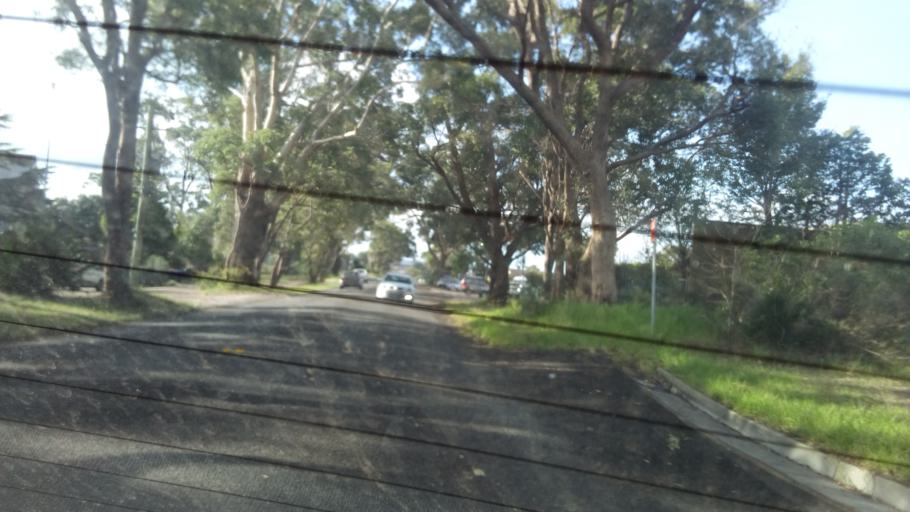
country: AU
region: New South Wales
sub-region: Wollongong
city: Helensburgh
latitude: -34.1973
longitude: 150.9740
